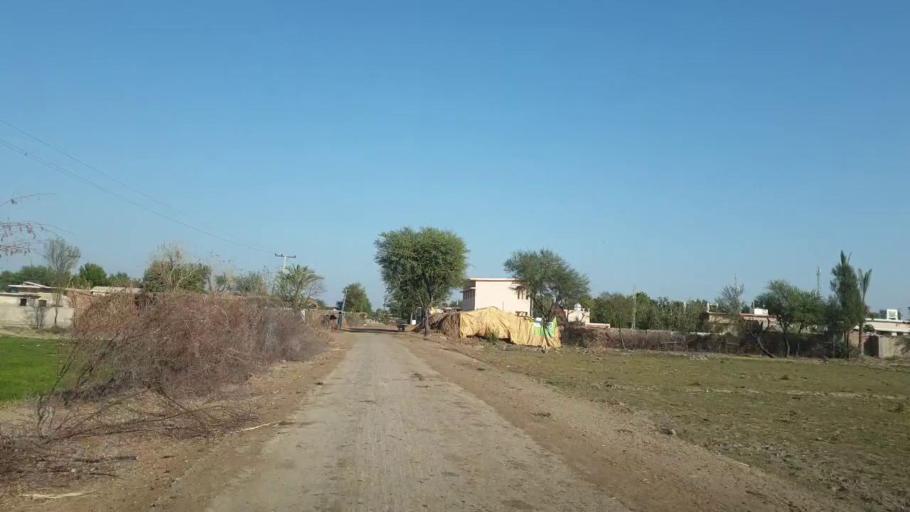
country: PK
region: Sindh
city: Mirpur Khas
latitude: 25.6191
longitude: 69.0768
